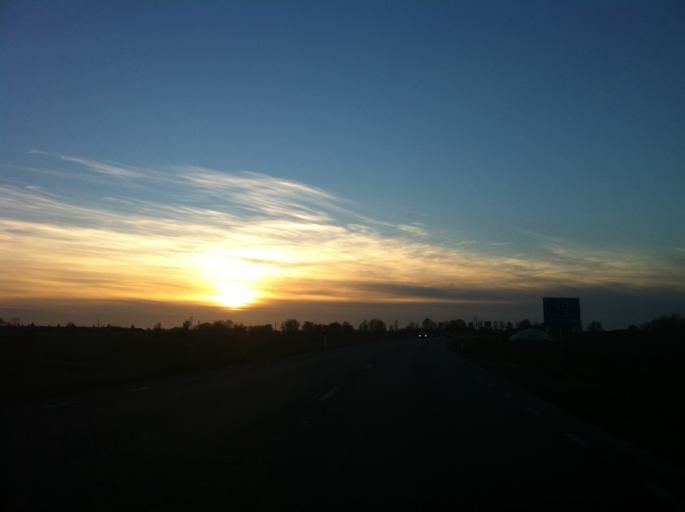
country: SE
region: Skane
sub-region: Svalovs Kommun
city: Svaloev
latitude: 55.8751
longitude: 13.1681
